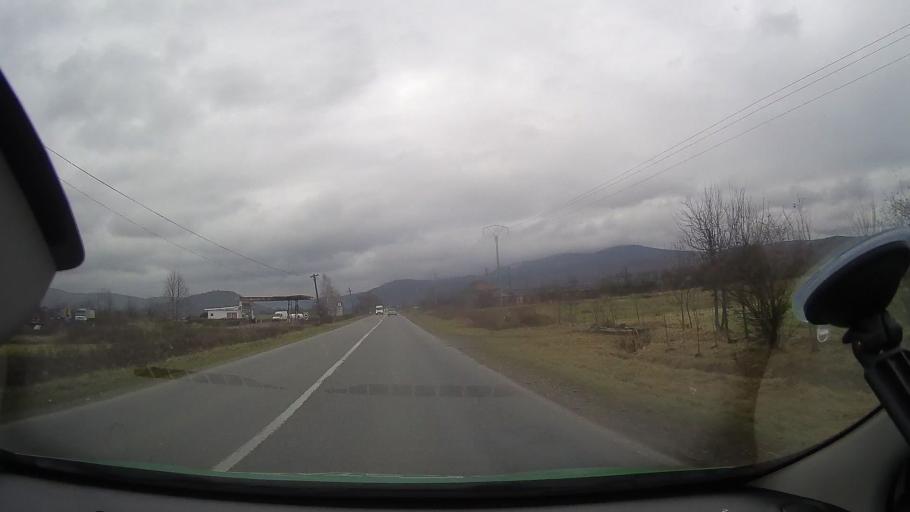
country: RO
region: Arad
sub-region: Comuna Buteni
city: Buteni
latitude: 46.3218
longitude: 22.1289
